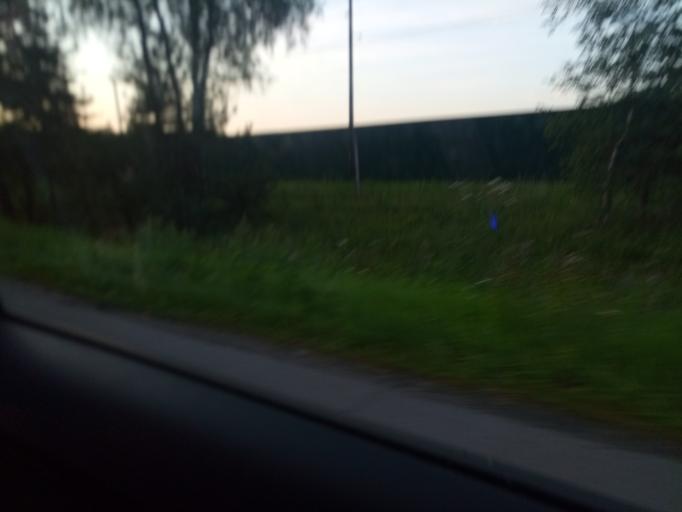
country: RU
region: Moskovskaya
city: Noginsk-9
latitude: 56.0515
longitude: 38.4545
